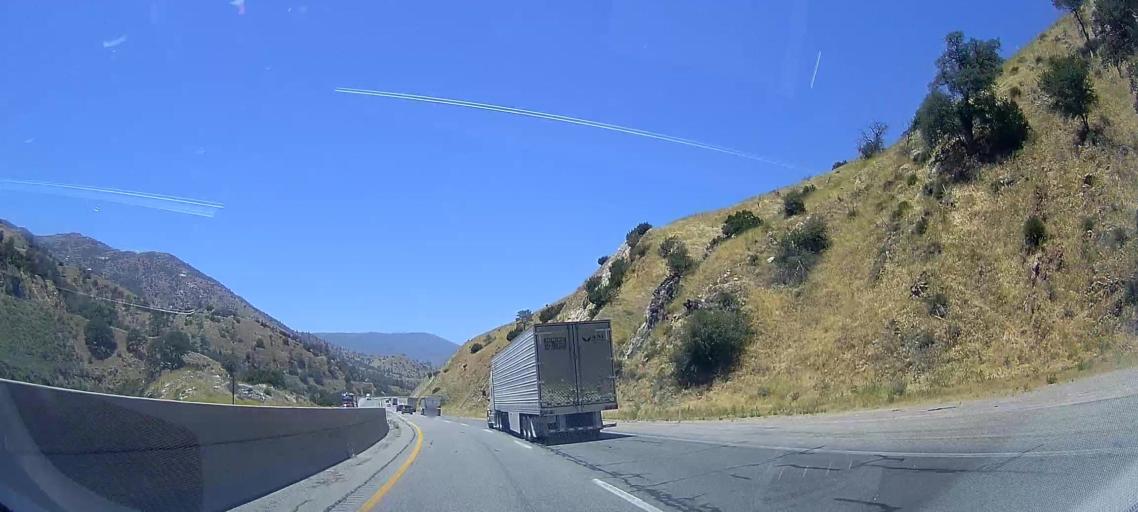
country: US
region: California
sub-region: Kern County
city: Golden Hills
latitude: 35.1814
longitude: -118.4898
